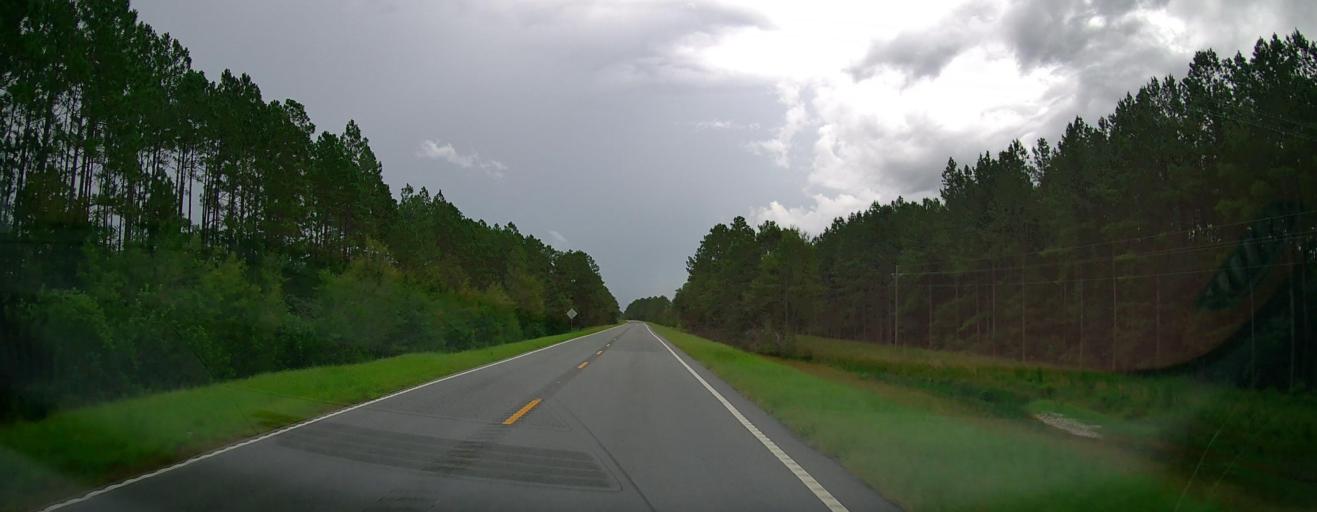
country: US
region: Georgia
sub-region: Brantley County
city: Nahunta
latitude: 31.3500
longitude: -82.0284
